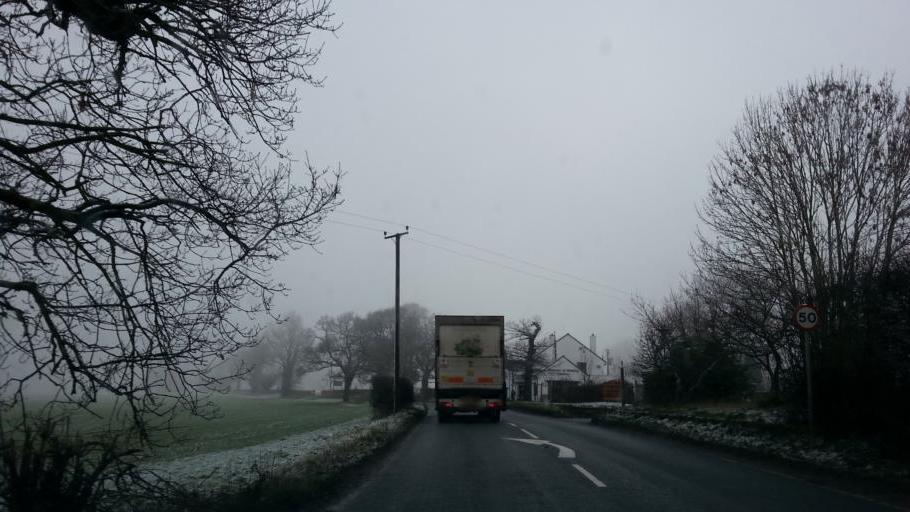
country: GB
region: England
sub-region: Cheshire East
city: Eaton
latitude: 53.1891
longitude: -2.2158
